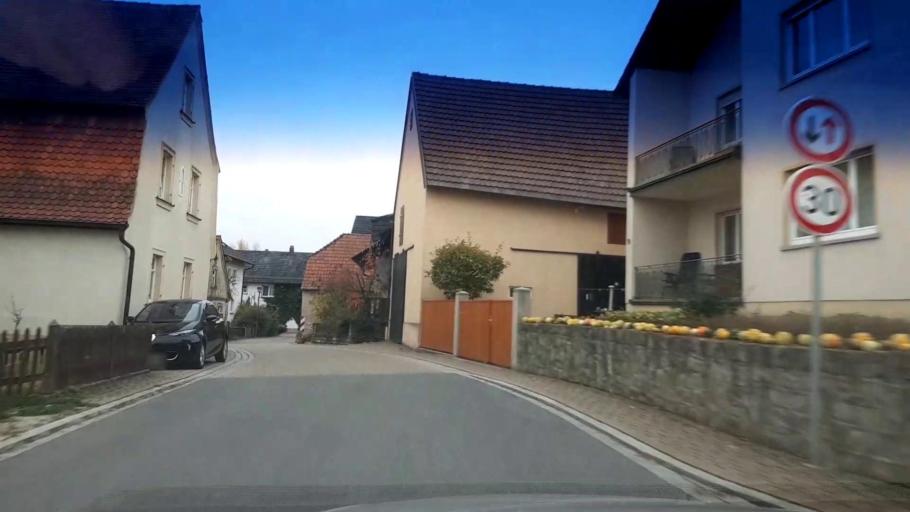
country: DE
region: Bavaria
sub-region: Upper Franconia
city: Rattelsdorf
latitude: 50.0049
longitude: 10.8739
